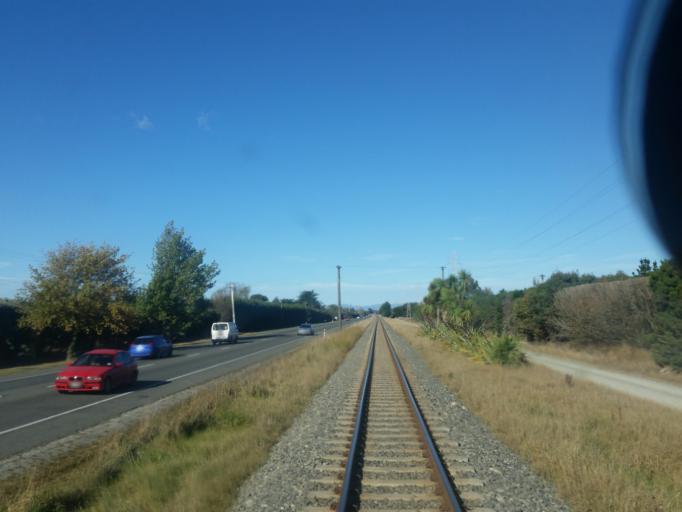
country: NZ
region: Canterbury
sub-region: Waimakariri District
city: Kaiapoi
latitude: -43.3475
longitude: 172.6194
